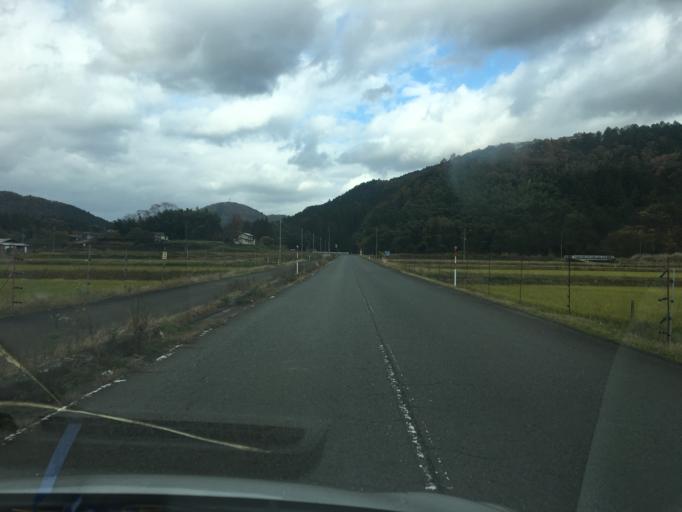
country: JP
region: Hyogo
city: Toyooka
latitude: 35.4749
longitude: 134.7182
